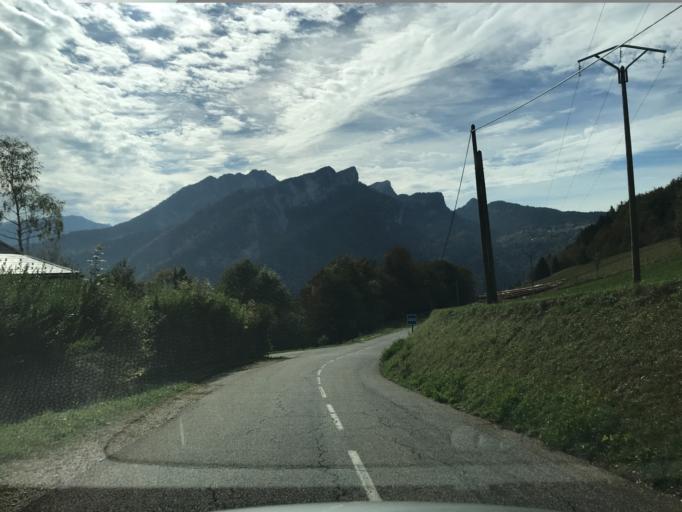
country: FR
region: Rhone-Alpes
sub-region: Departement de la Savoie
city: Les Echelles
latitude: 45.4357
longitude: 5.8300
